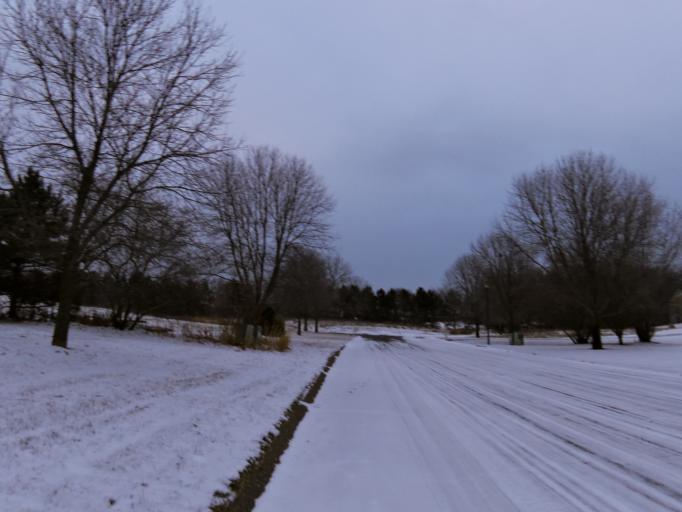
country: US
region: Minnesota
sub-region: Washington County
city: Lakeland
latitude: 44.9586
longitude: -92.8186
